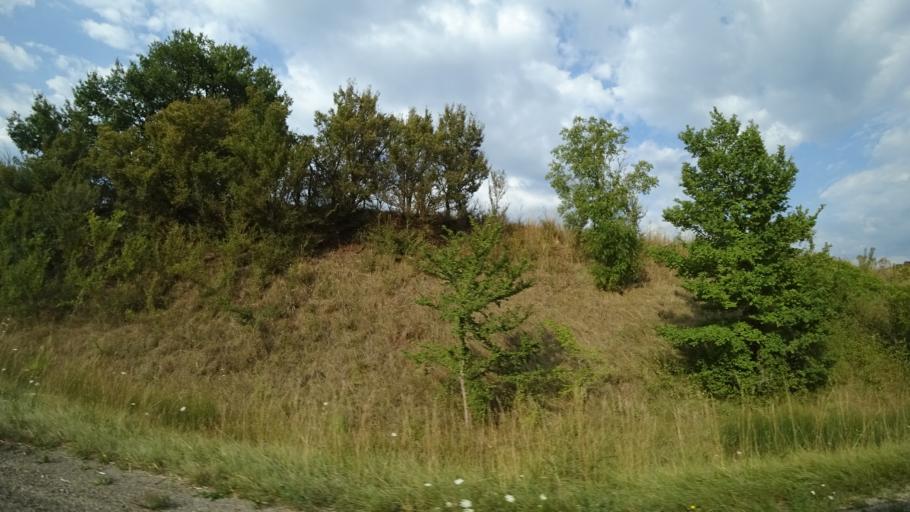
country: FR
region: Midi-Pyrenees
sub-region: Departement de l'Aveyron
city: Saint-Christophe-Vallon
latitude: 44.4778
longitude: 2.4069
